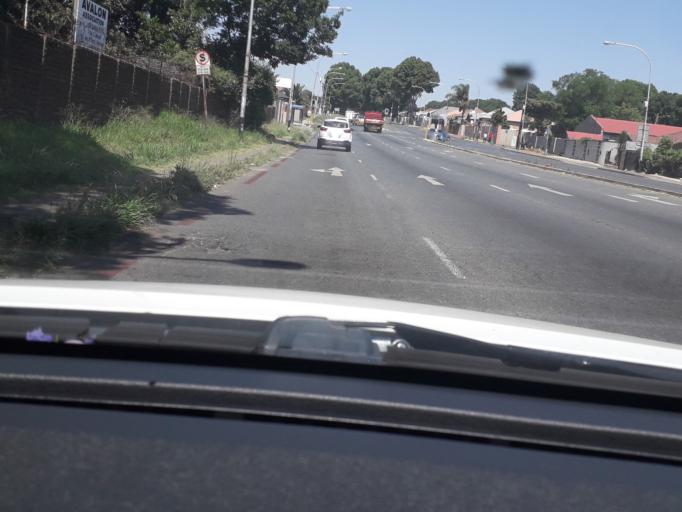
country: ZA
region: Gauteng
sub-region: City of Johannesburg Metropolitan Municipality
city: Johannesburg
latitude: -26.1863
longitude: 28.0991
